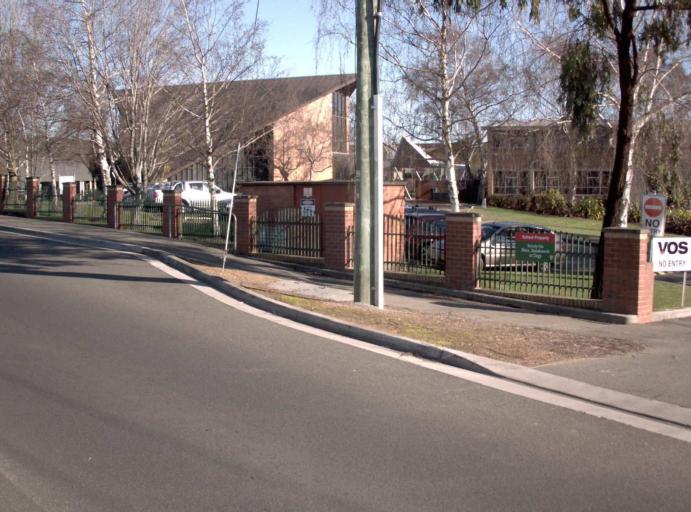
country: AU
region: Tasmania
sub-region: Launceston
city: Summerhill
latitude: -41.4735
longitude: 147.1288
